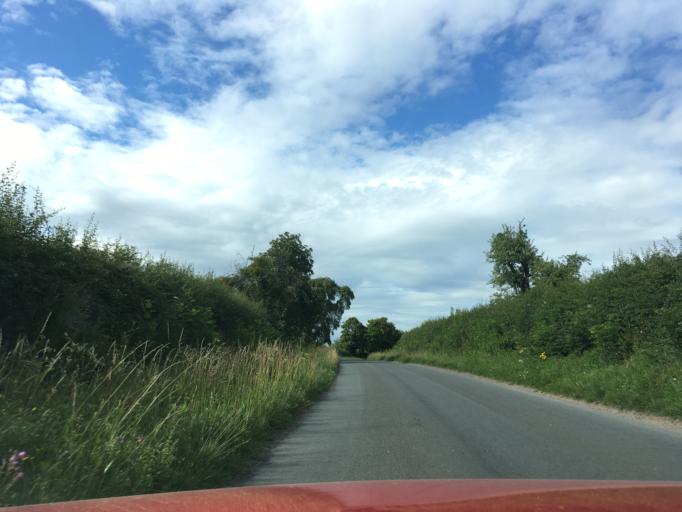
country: GB
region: England
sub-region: Gloucestershire
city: Stonehouse
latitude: 51.7904
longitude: -2.2725
